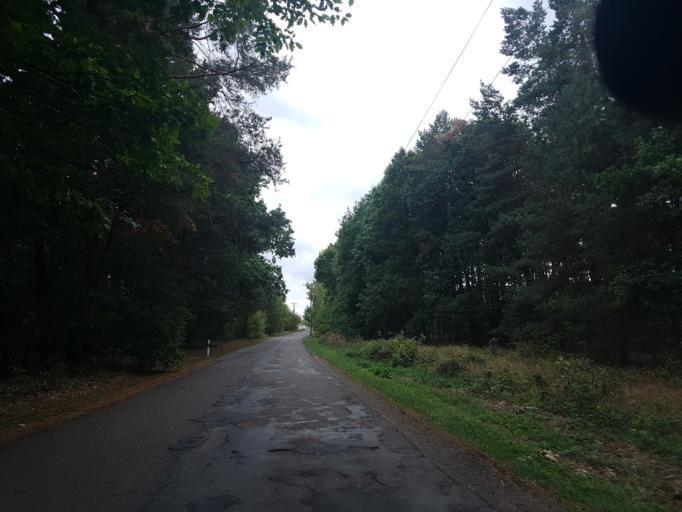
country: DE
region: Saxony-Anhalt
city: Rosslau
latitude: 51.9649
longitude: 12.3001
